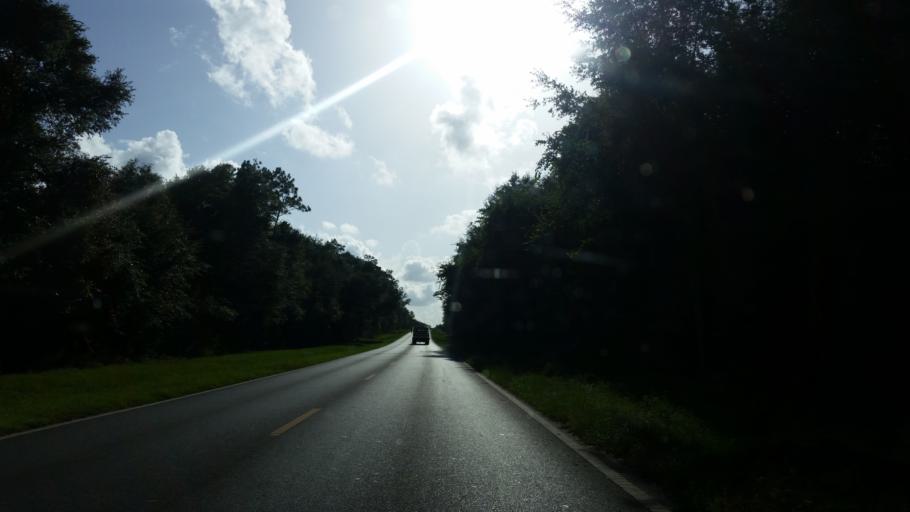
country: US
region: Florida
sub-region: Santa Rosa County
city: Bagdad
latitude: 30.5877
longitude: -87.0679
